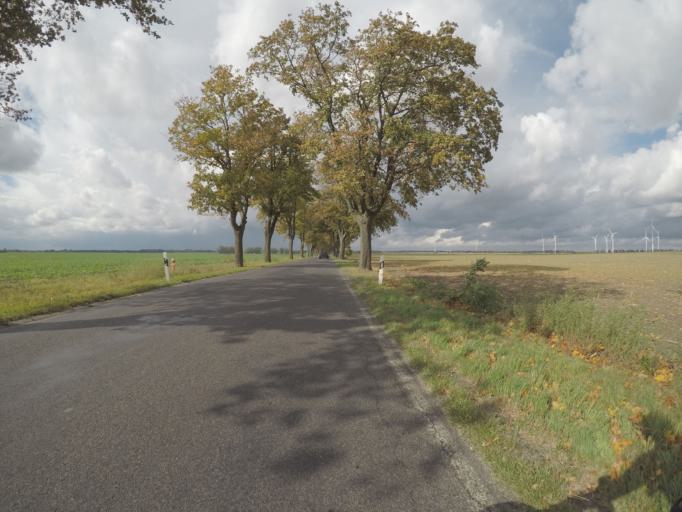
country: DE
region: Brandenburg
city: Altlandsberg
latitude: 52.5882
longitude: 13.7814
